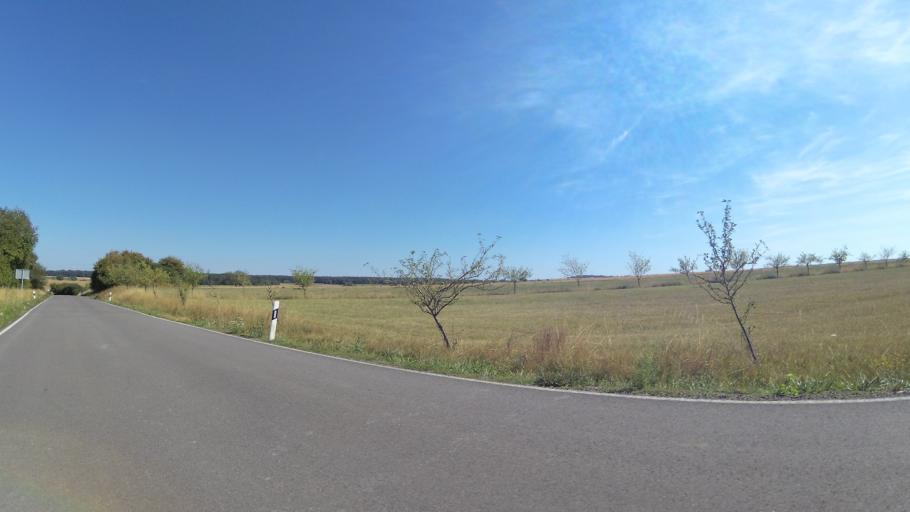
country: DE
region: Rheinland-Pfalz
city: Hornbach
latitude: 49.1692
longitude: 7.3022
